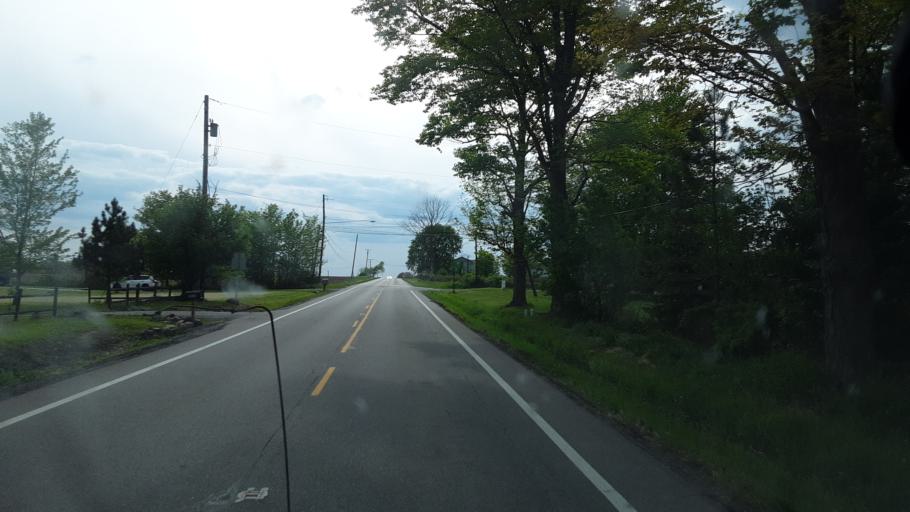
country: US
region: Ohio
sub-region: Portage County
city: Windham
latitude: 41.2350
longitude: -81.0838
